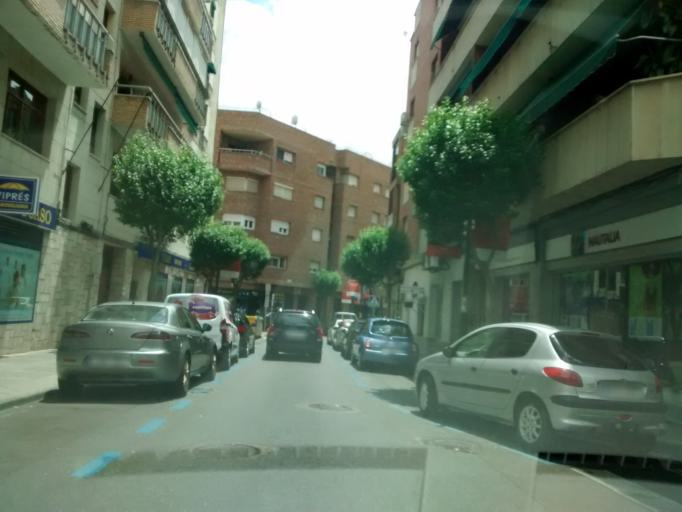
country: ES
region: Extremadura
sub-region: Provincia de Badajoz
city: Merida
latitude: 38.9187
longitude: -6.3438
